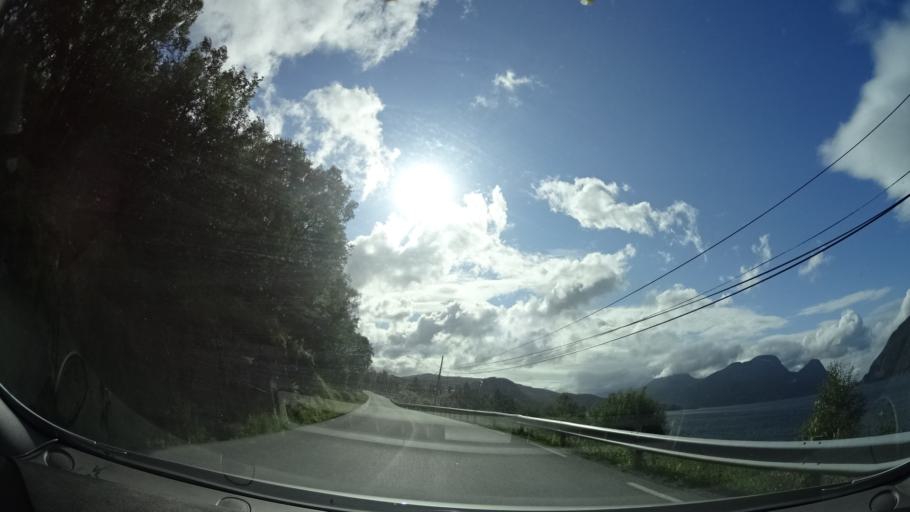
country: NO
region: More og Romsdal
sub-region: Halsa
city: Liaboen
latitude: 63.1343
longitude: 8.3991
